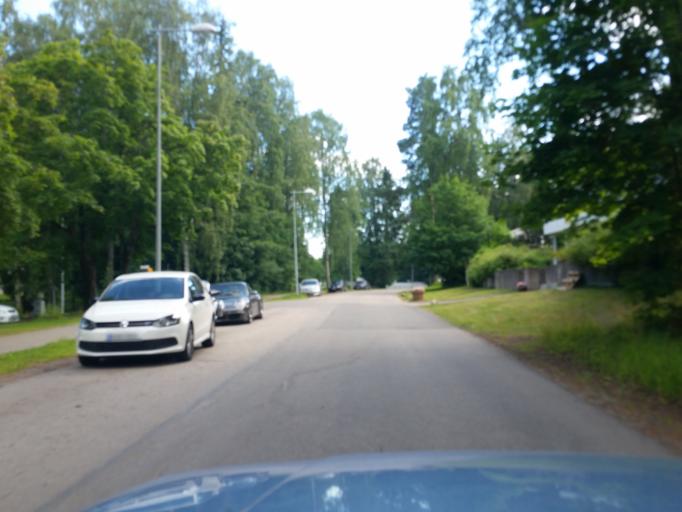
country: FI
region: Uusimaa
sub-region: Helsinki
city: Koukkuniemi
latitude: 60.1717
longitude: 24.7928
